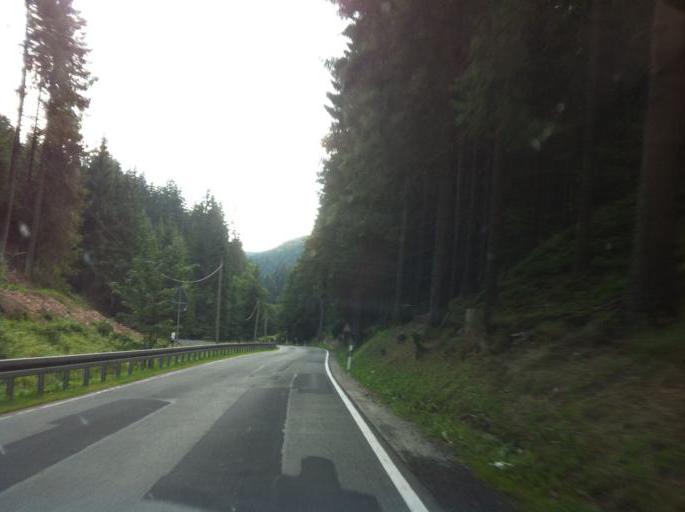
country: DE
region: Thuringia
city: Steinheid
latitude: 50.4688
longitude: 11.0708
